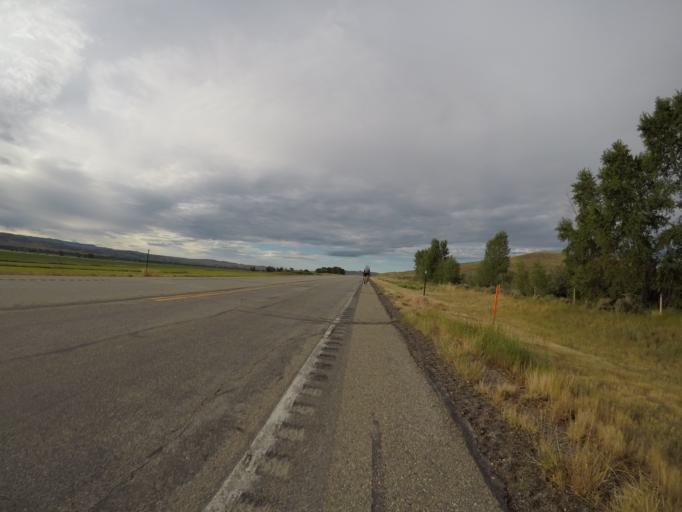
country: US
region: Wyoming
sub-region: Carbon County
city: Saratoga
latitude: 41.3793
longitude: -106.7492
